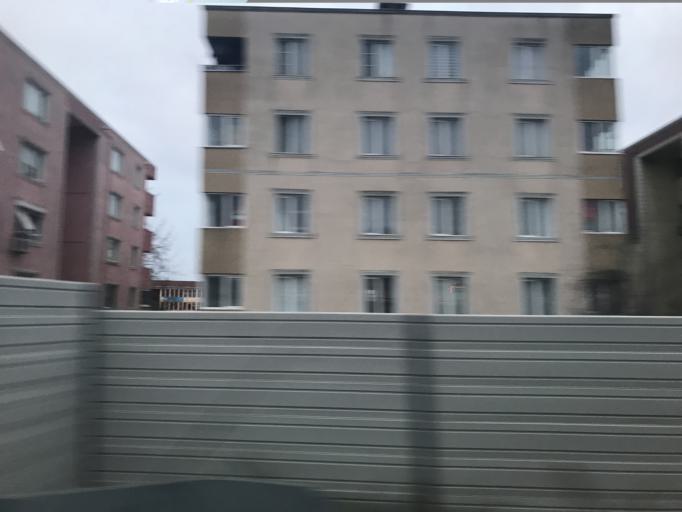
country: TR
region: Istanbul
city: Icmeler
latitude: 40.8419
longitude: 29.3050
